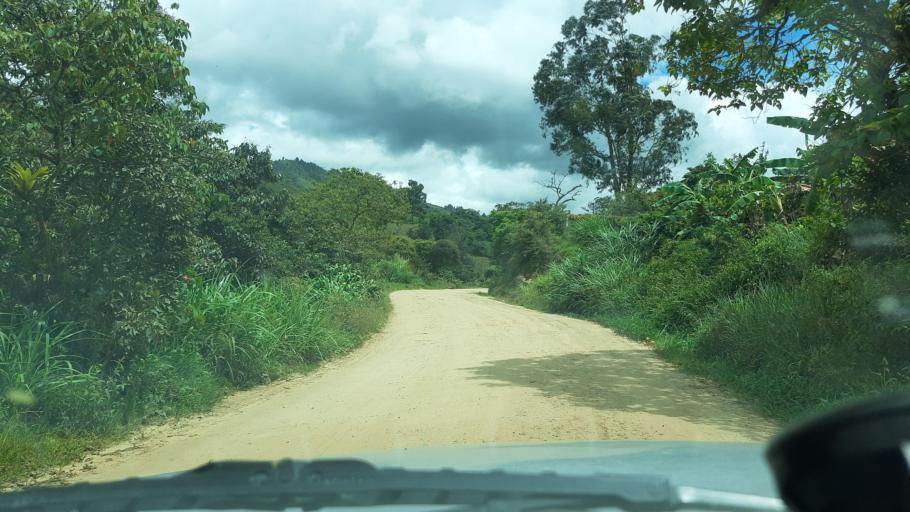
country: CO
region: Cundinamarca
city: Umbita
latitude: 5.2237
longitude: -73.4130
